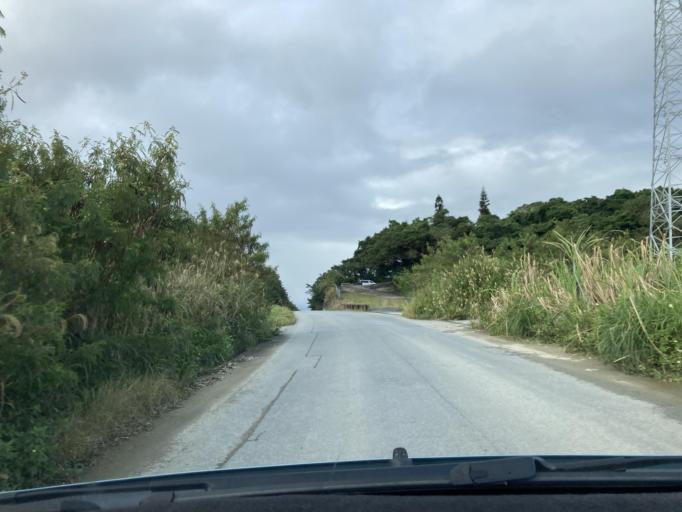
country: JP
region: Okinawa
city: Itoman
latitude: 26.1212
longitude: 127.6863
